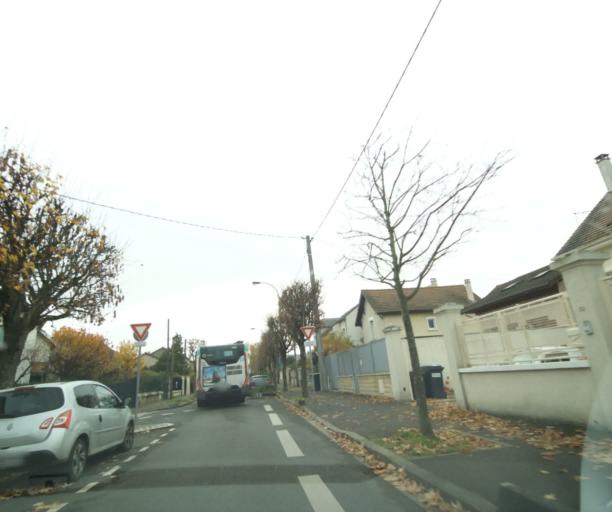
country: FR
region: Ile-de-France
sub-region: Departement de Seine-Saint-Denis
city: Villemomble
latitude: 48.8872
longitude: 2.4988
